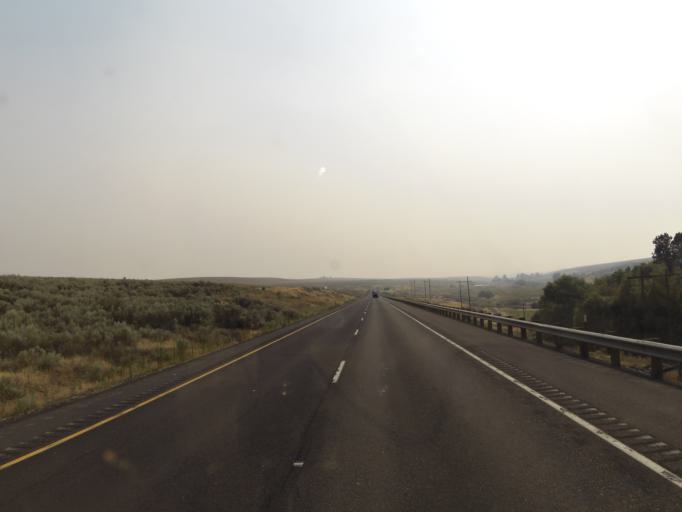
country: US
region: Washington
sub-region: Adams County
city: Ritzville
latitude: 47.0340
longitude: -118.4609
